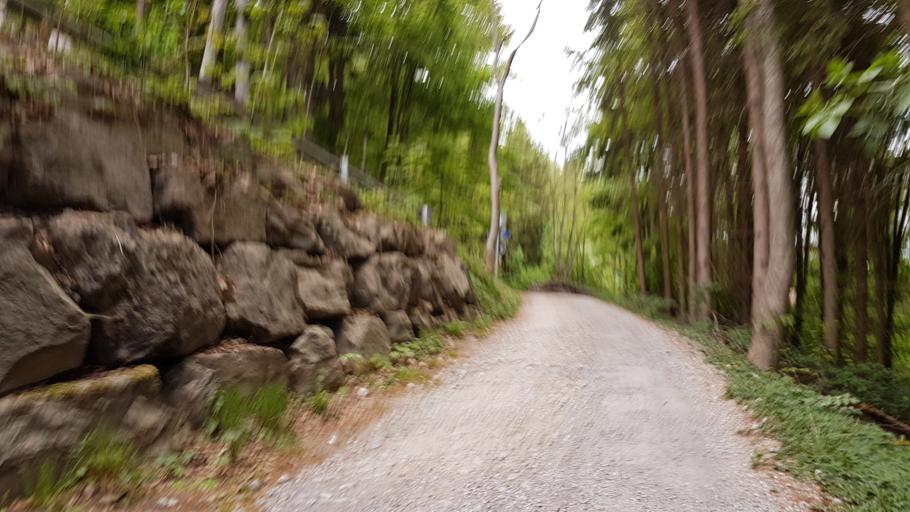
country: CH
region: Bern
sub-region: Bern-Mittelland District
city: Munsingen
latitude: 46.8644
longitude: 7.5466
